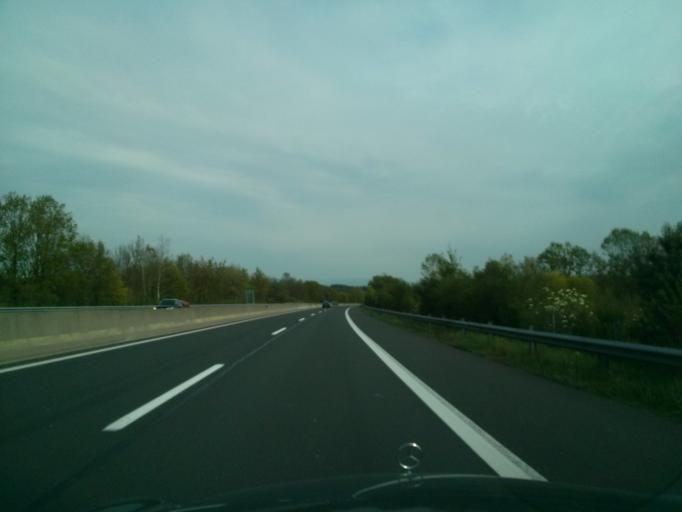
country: AT
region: Styria
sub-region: Politischer Bezirk Hartberg-Fuerstenfeld
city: Sebersdorf
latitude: 47.2006
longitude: 15.9907
